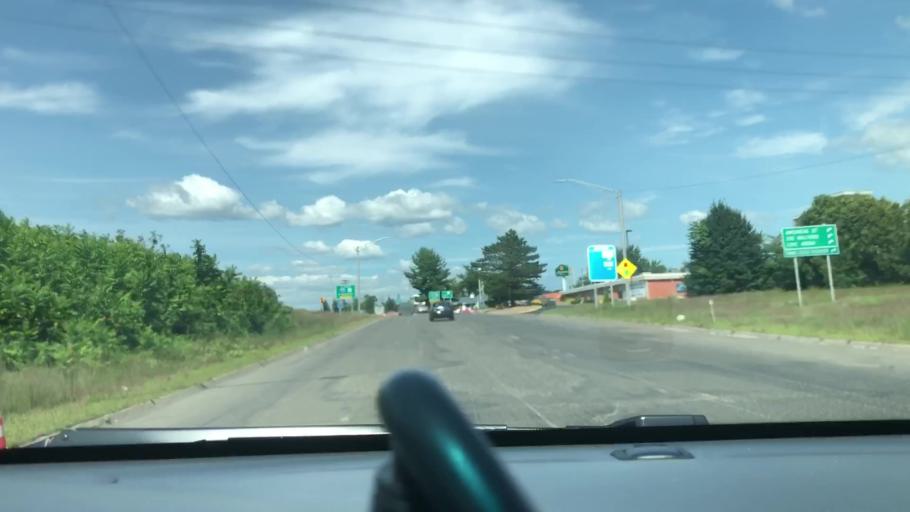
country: US
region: New Hampshire
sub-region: Hillsborough County
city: Manchester
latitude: 43.0030
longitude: -71.4741
